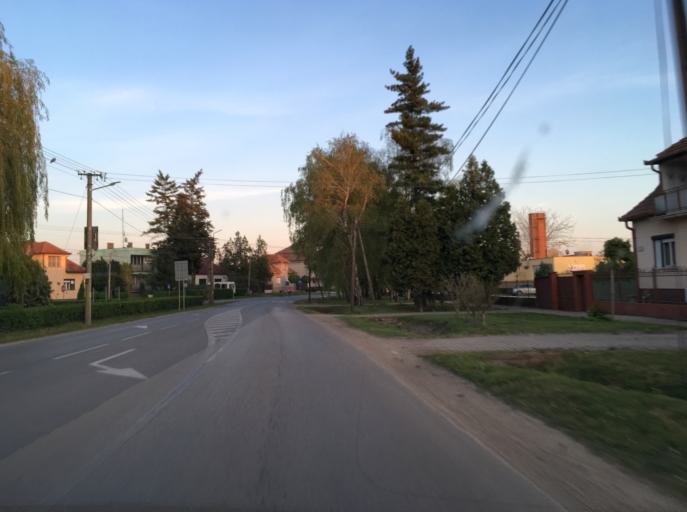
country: SK
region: Nitriansky
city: Kolarovo
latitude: 47.9146
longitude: 17.9994
